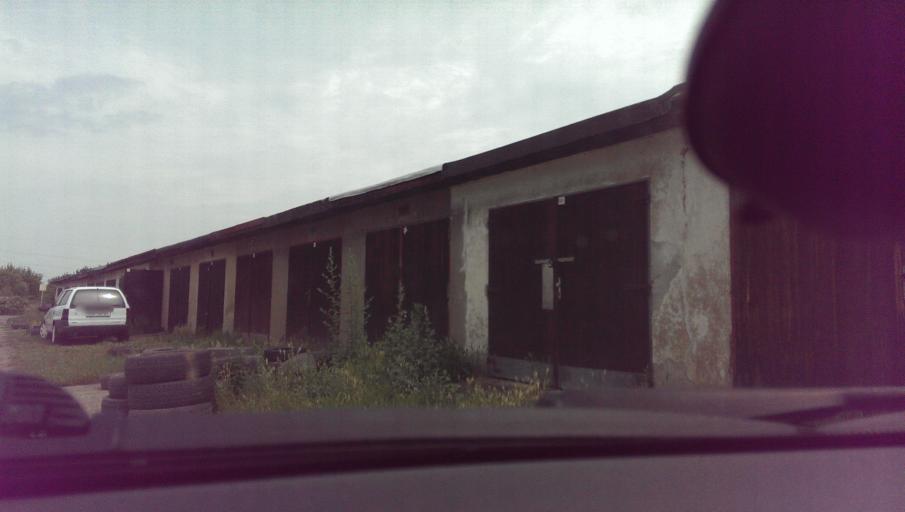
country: CZ
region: Zlin
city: Tecovice
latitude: 49.2097
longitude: 17.5786
